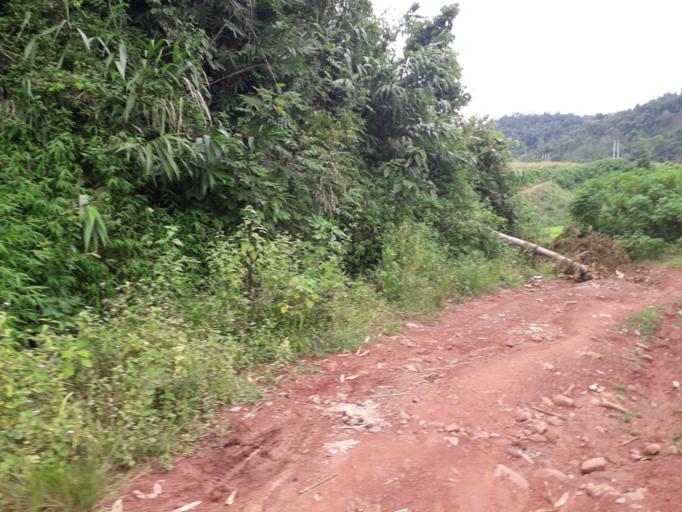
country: CN
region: Yunnan
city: Menglie
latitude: 22.2052
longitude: 101.6659
